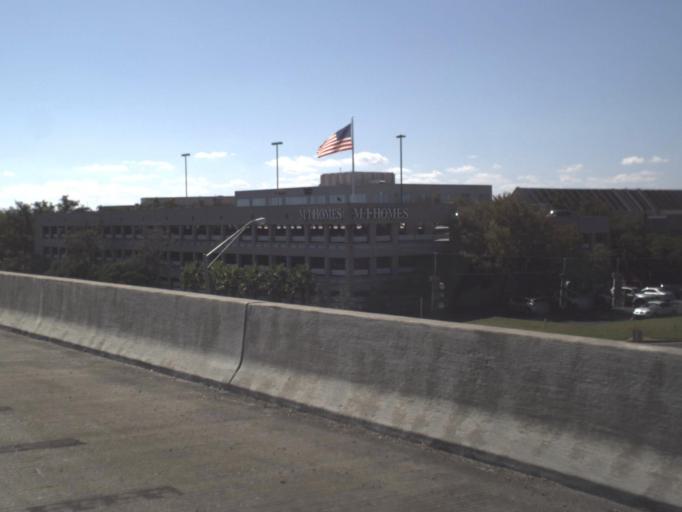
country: US
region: Florida
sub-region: Hillsborough County
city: Town 'n' Country
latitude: 27.9819
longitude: -82.5466
